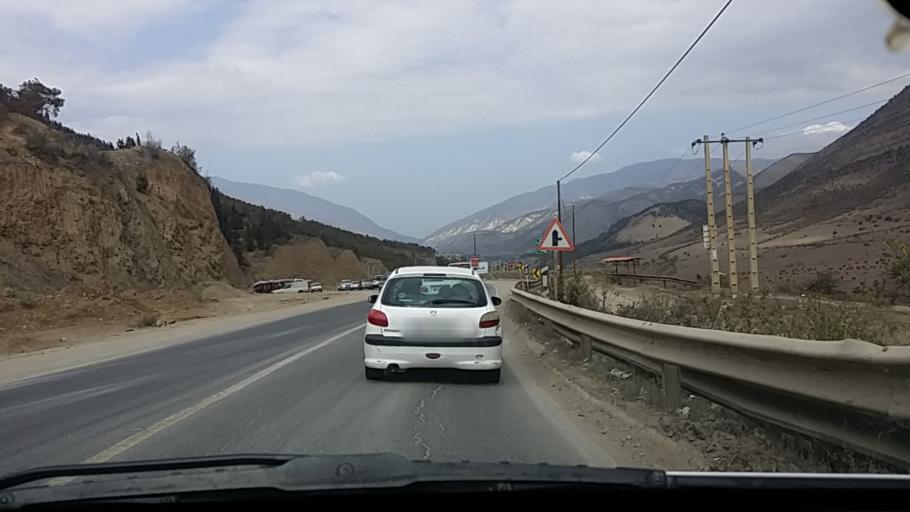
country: IR
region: Mazandaran
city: Chalus
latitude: 36.4266
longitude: 51.2843
